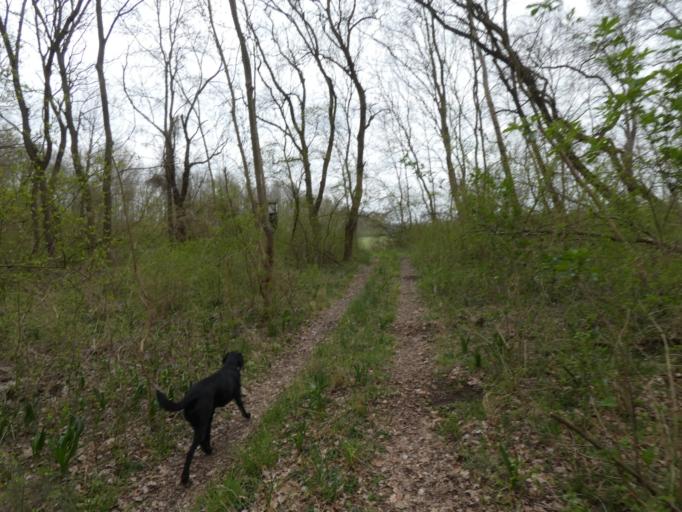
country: HU
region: Pest
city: Ocsa
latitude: 47.2582
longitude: 19.2488
